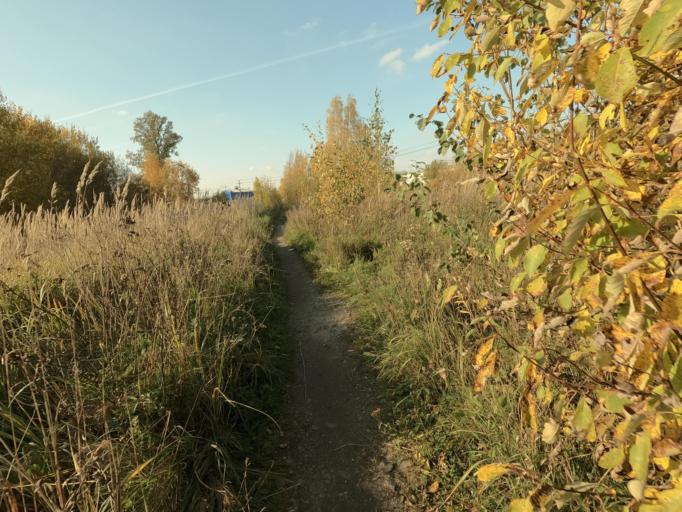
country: RU
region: Leningrad
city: Mga
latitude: 59.7533
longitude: 31.0662
